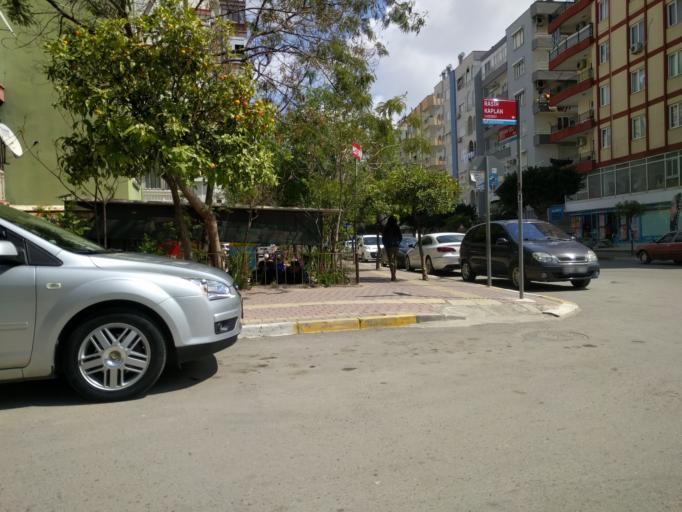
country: TR
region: Antalya
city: Antalya
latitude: 36.9079
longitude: 30.6843
